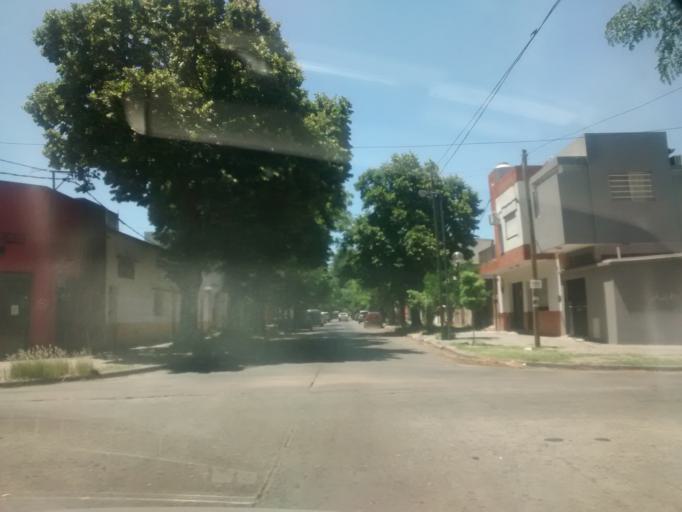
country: AR
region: Buenos Aires
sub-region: Partido de La Plata
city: La Plata
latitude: -34.9419
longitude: -57.9501
